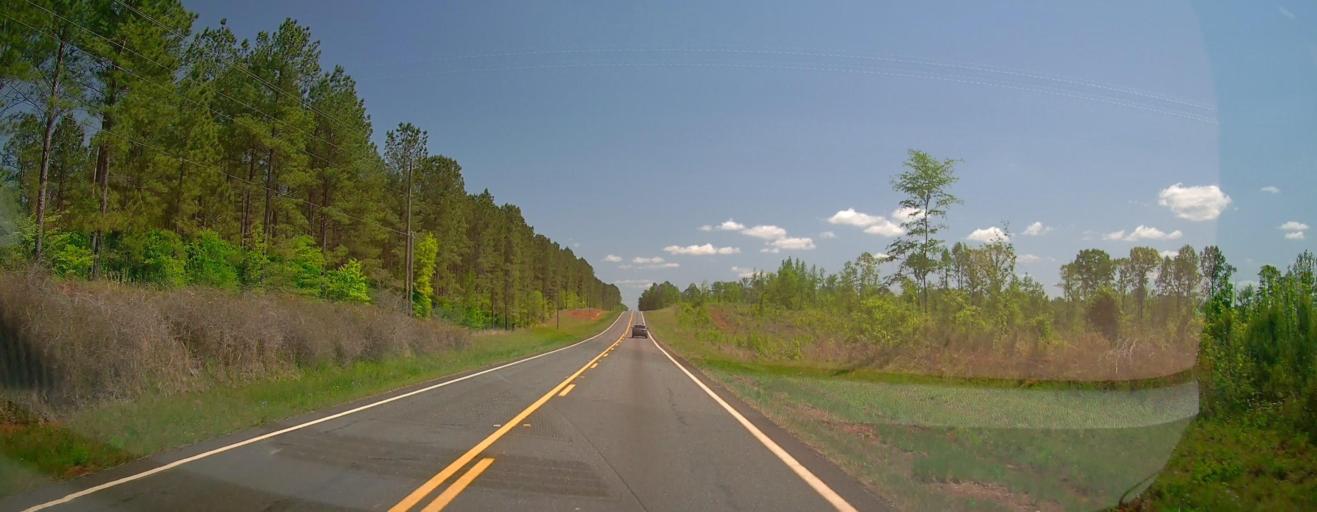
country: US
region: Georgia
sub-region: Jasper County
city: Monticello
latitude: 33.2601
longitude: -83.5725
